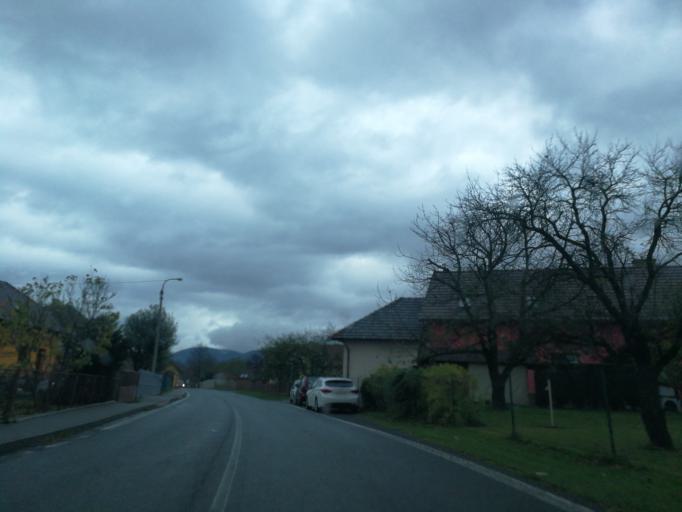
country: CZ
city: Hodslavice
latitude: 49.5372
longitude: 18.0262
